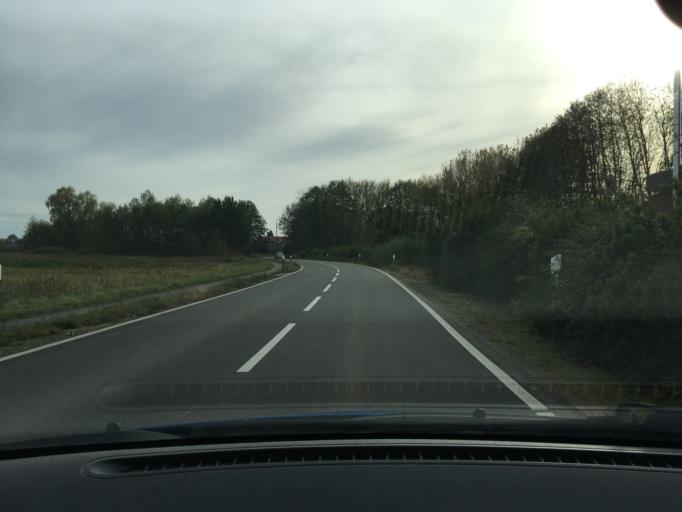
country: DE
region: Lower Saxony
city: Bardowick
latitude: 53.3116
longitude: 10.3865
